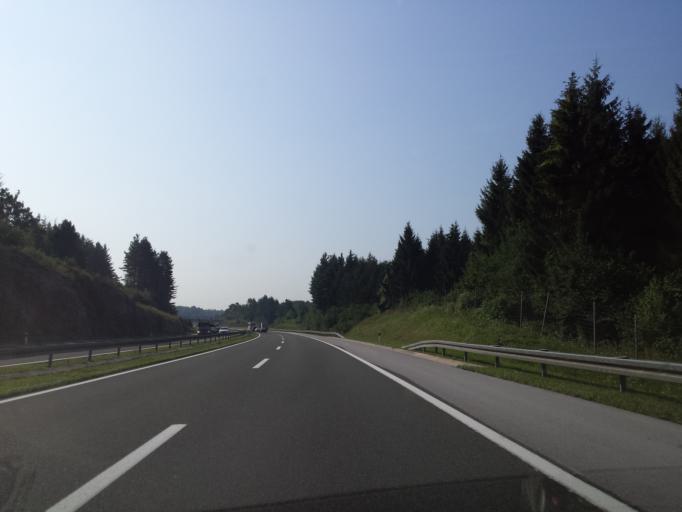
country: HR
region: Karlovacka
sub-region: Grad Ogulin
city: Ogulin
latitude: 45.3856
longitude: 15.2603
